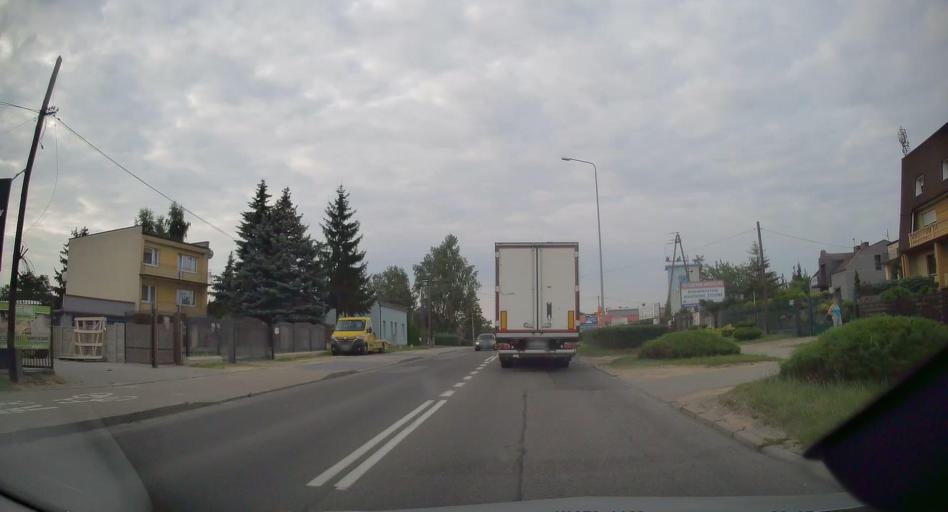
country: PL
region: Lodz Voivodeship
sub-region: Powiat radomszczanski
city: Radomsko
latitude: 51.0551
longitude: 19.4404
